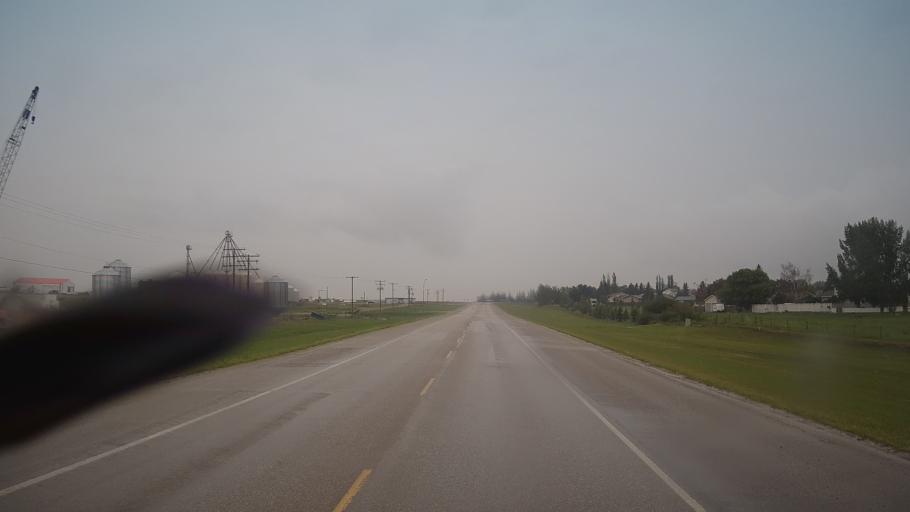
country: CA
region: Saskatchewan
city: Biggar
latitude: 52.0600
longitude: -107.9991
